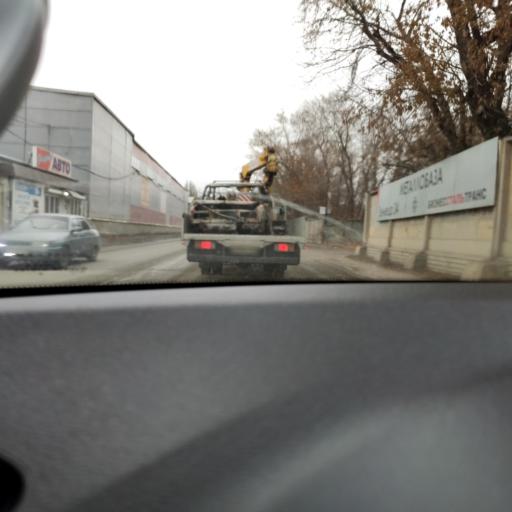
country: RU
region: Samara
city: Smyshlyayevka
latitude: 53.2088
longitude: 50.3010
